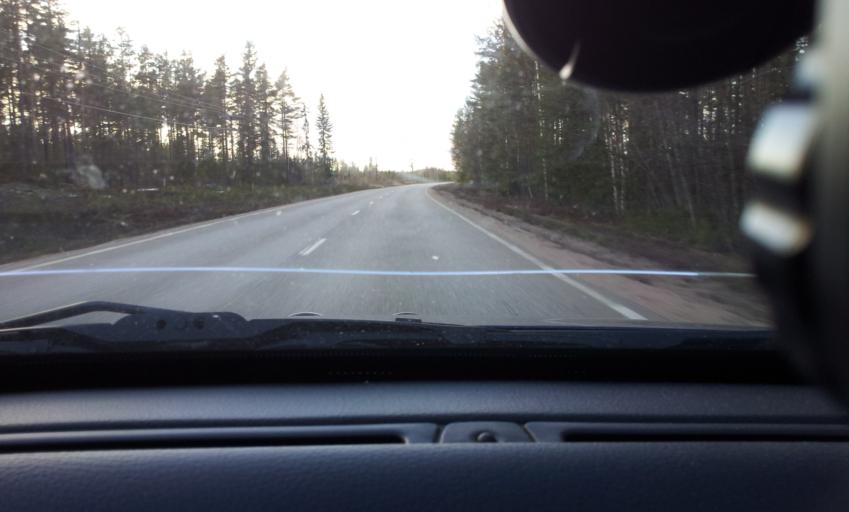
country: SE
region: Jaemtland
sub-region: Harjedalens Kommun
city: Sveg
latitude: 62.1005
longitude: 15.0733
